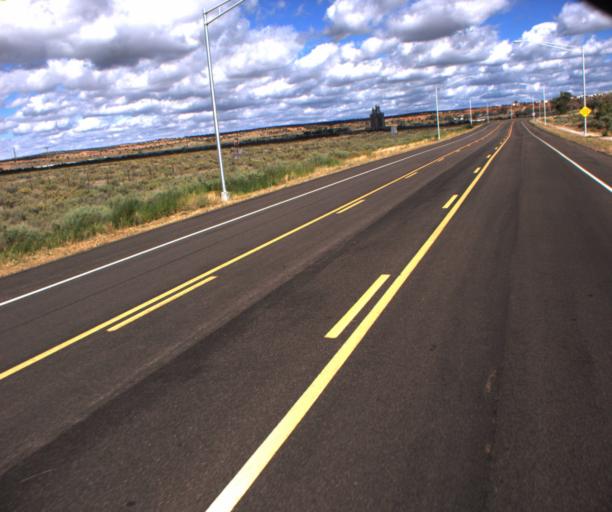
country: US
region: Arizona
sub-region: Apache County
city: Houck
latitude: 35.2008
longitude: -109.3327
